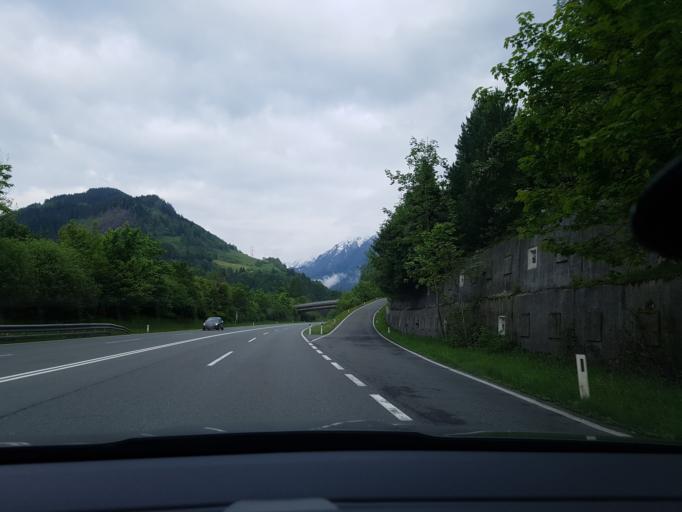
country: AT
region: Salzburg
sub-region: Politischer Bezirk Zell am See
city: Lend
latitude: 47.3066
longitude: 13.0228
